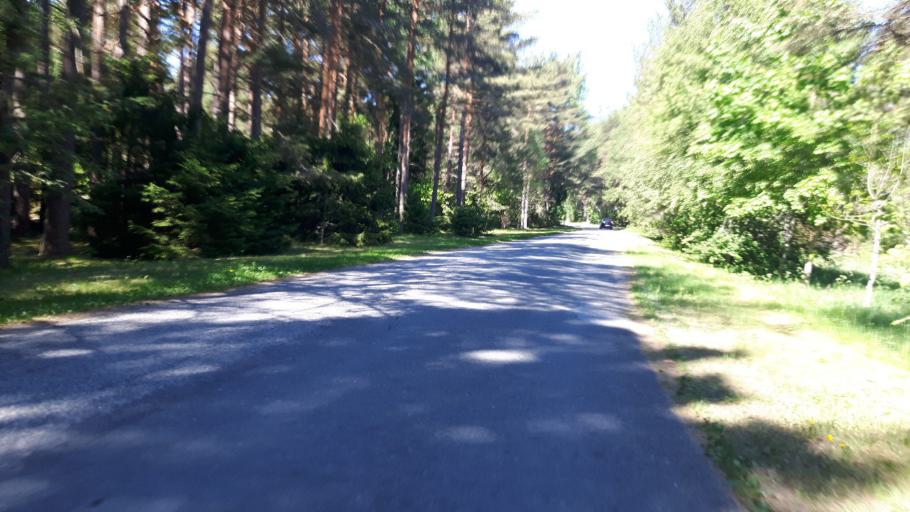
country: EE
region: Harju
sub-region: Loksa linn
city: Loksa
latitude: 59.5618
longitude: 25.6691
